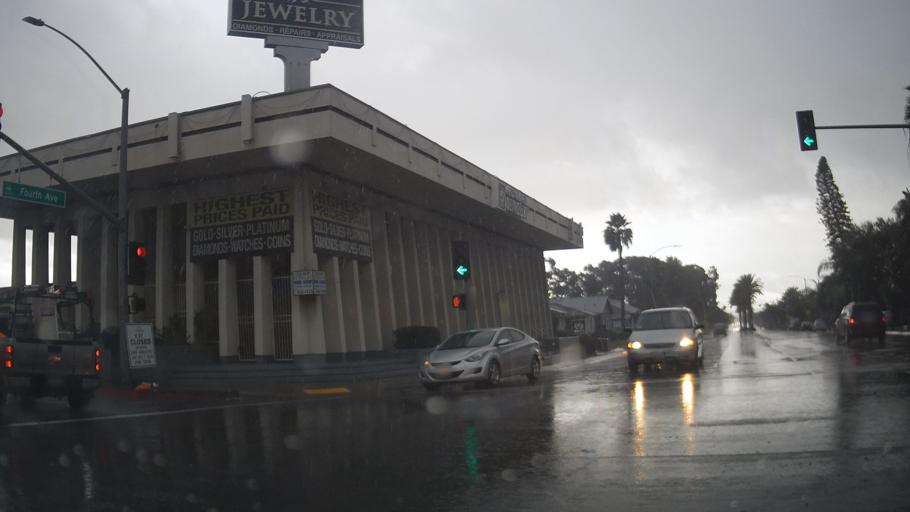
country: US
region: California
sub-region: San Diego County
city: Chula Vista
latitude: 32.6437
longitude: -117.0852
